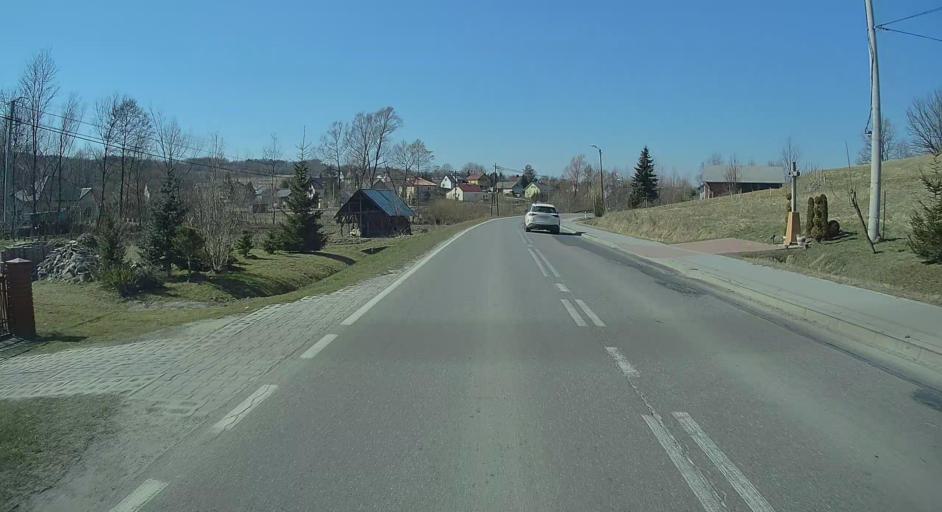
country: PL
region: Subcarpathian Voivodeship
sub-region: Powiat rzeszowski
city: Hyzne
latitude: 49.9149
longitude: 22.1854
